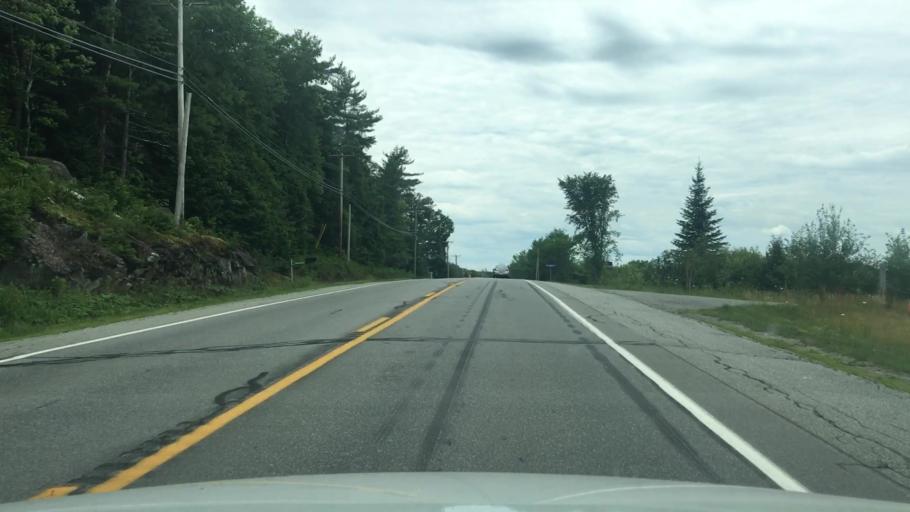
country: US
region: Maine
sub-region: Kennebec County
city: Augusta
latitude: 44.3313
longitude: -69.7219
